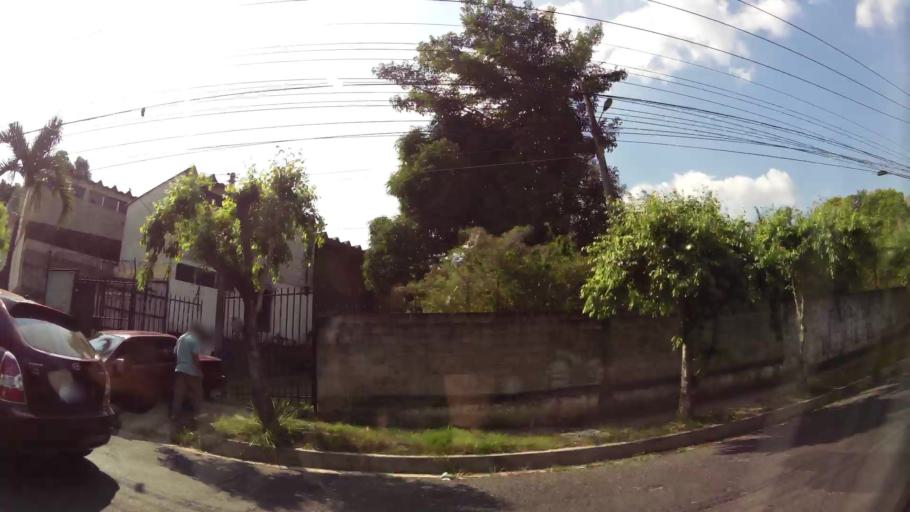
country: SV
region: San Salvador
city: Mejicanos
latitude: 13.7244
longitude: -89.2115
